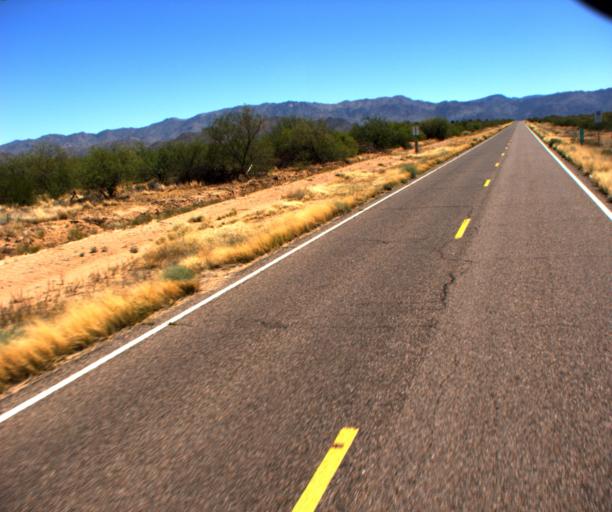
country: US
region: Arizona
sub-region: Yavapai County
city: Congress
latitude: 34.1487
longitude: -112.8869
